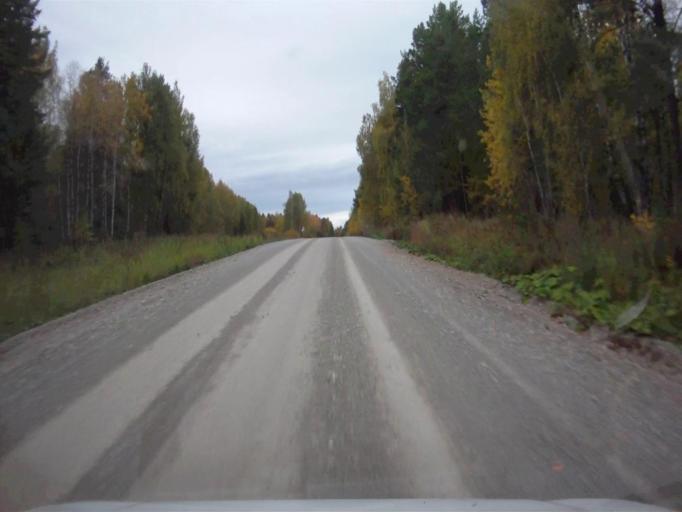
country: RU
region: Chelyabinsk
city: Nyazepetrovsk
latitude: 56.0788
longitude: 59.4242
